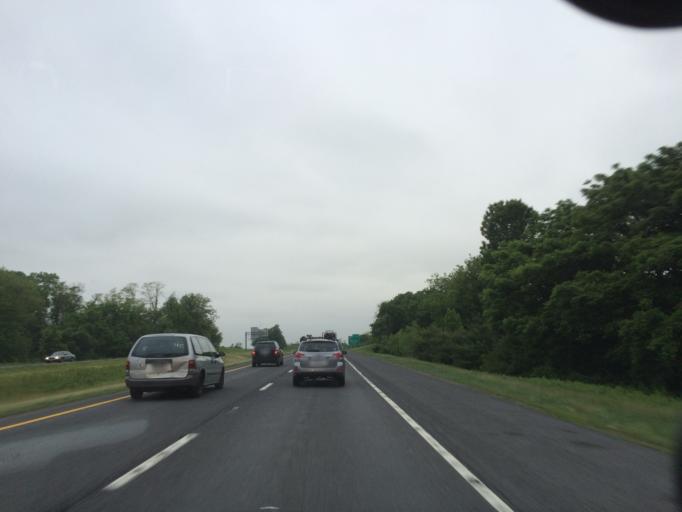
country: US
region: Maryland
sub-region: Washington County
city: Halfway
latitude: 39.6065
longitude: -77.7649
